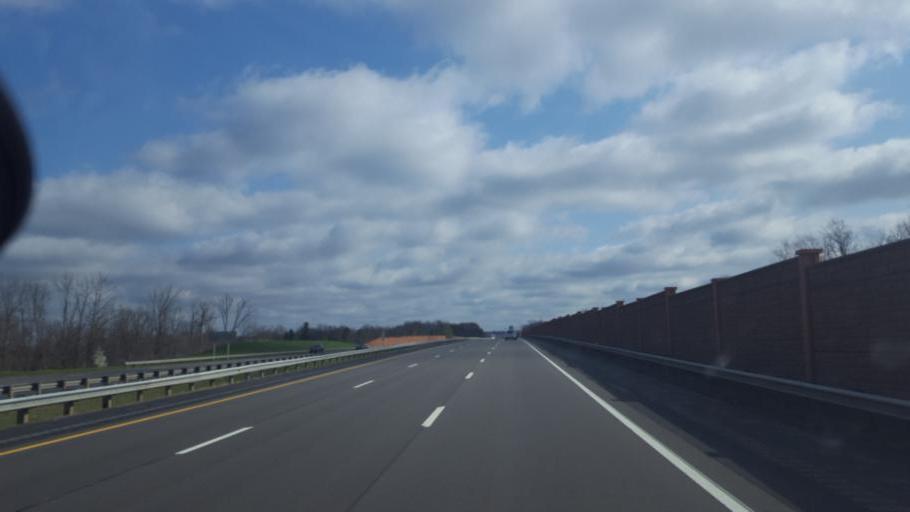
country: US
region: Ohio
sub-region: Medina County
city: Medina
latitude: 41.1174
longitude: -81.8076
